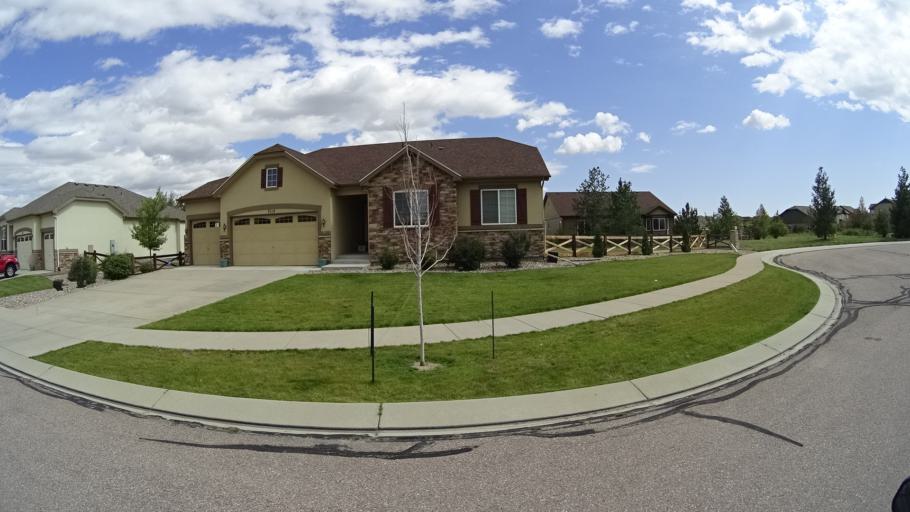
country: US
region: Colorado
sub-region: El Paso County
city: Cimarron Hills
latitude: 38.9351
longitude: -104.6799
